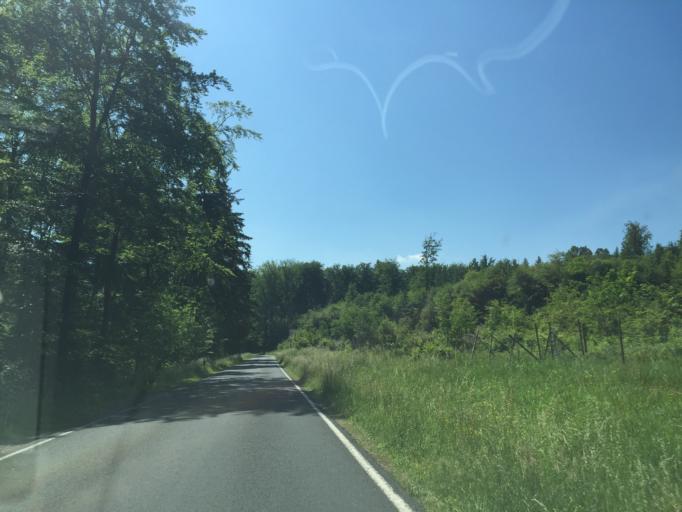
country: DE
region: Bavaria
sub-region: Regierungsbezirk Unterfranken
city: Eichenbuhl
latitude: 49.6514
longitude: 9.3087
